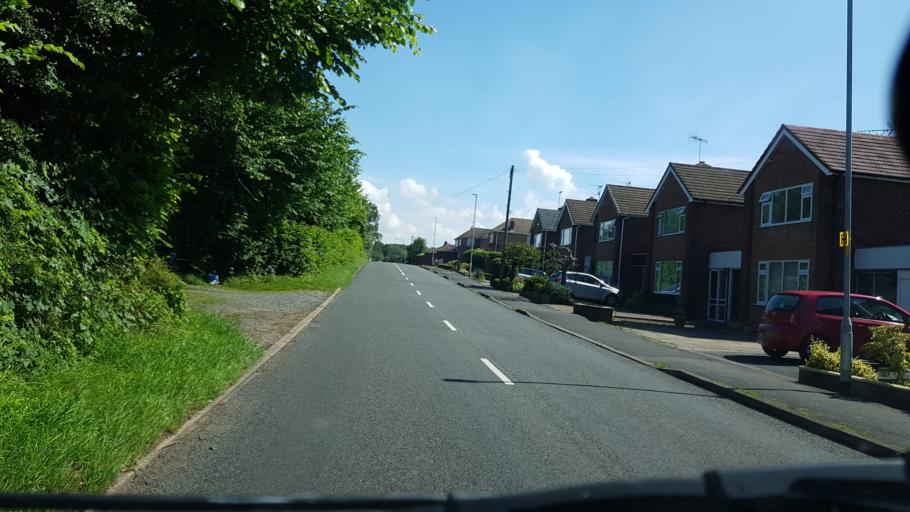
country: GB
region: England
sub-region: Worcestershire
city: Stourport-on-Severn
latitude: 52.3523
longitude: -2.2957
